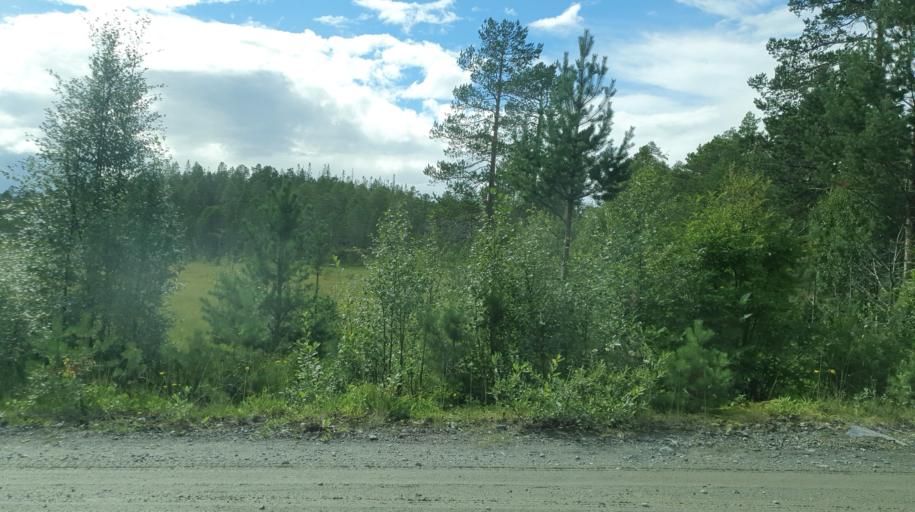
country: NO
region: Nord-Trondelag
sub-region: Levanger
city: Skogn
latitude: 63.5832
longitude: 11.2453
